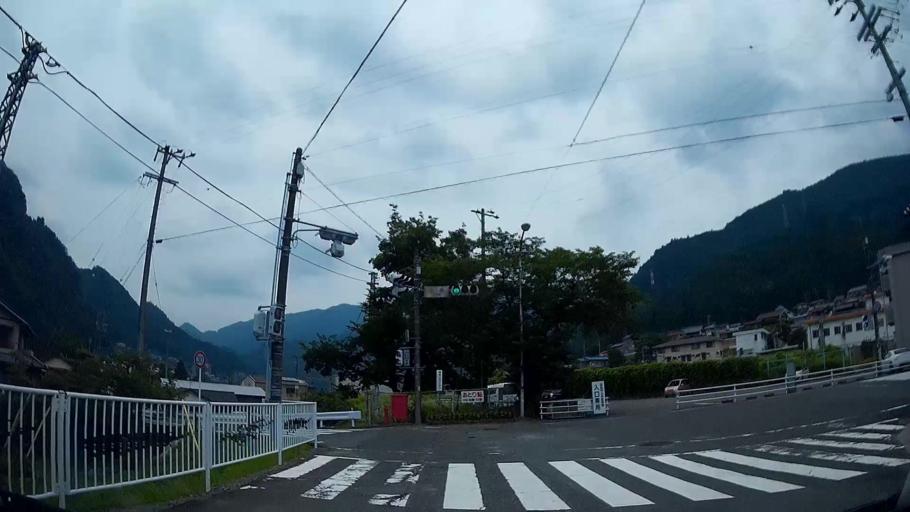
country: JP
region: Shizuoka
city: Mori
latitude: 35.0860
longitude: 137.8017
